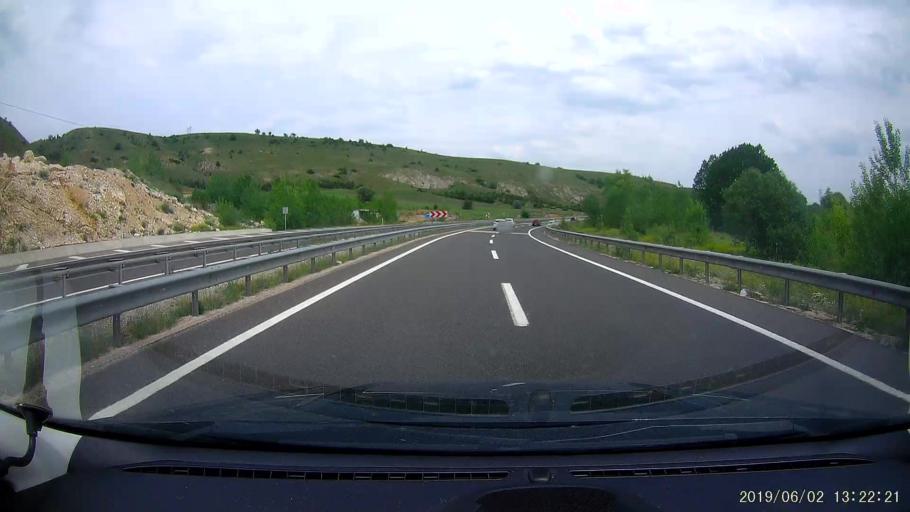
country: TR
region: Cankiri
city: Cerkes
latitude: 40.8265
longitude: 32.7971
